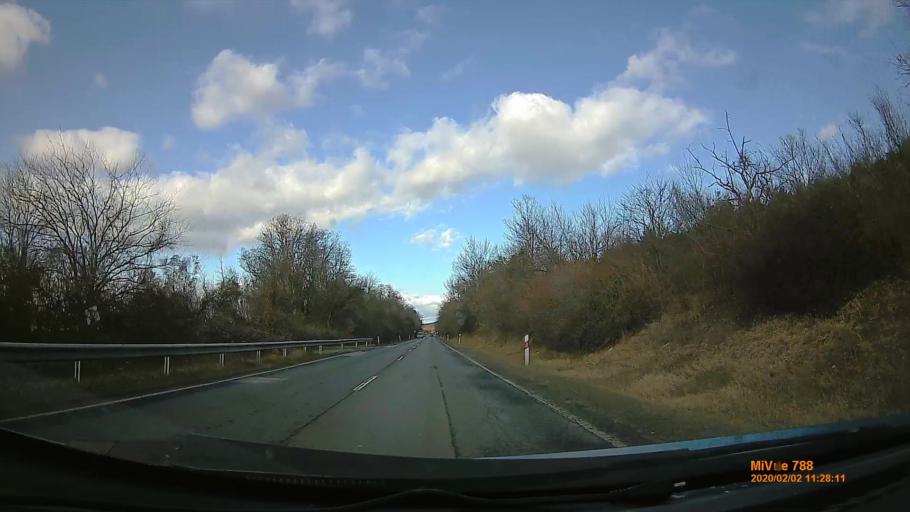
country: AT
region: Burgenland
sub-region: Eisenstadt-Umgebung
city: Klingenbach
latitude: 47.7249
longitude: 16.5609
